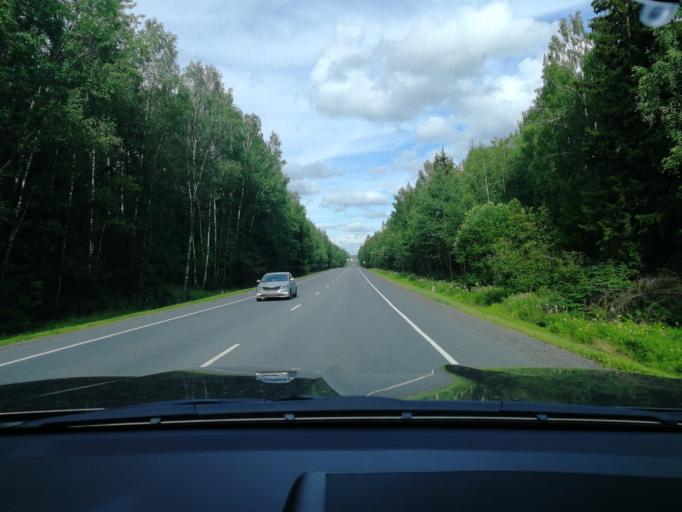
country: RU
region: Moskovskaya
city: Popovo
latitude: 55.0433
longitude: 37.7030
